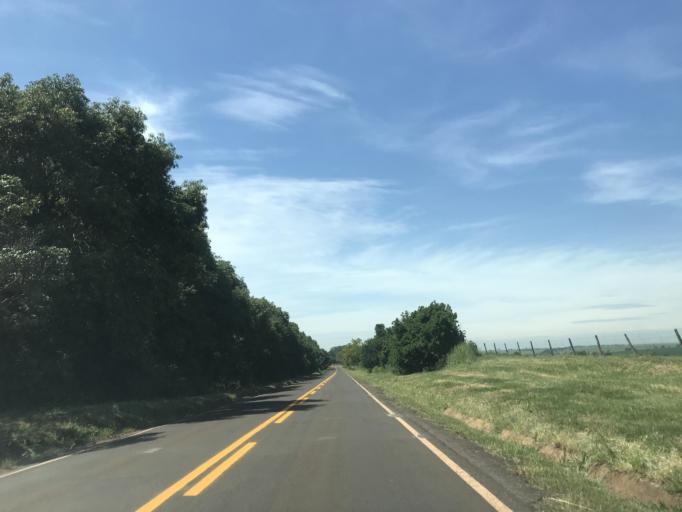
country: BR
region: Parana
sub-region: Terra Rica
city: Terra Rica
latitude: -22.7880
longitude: -52.6553
